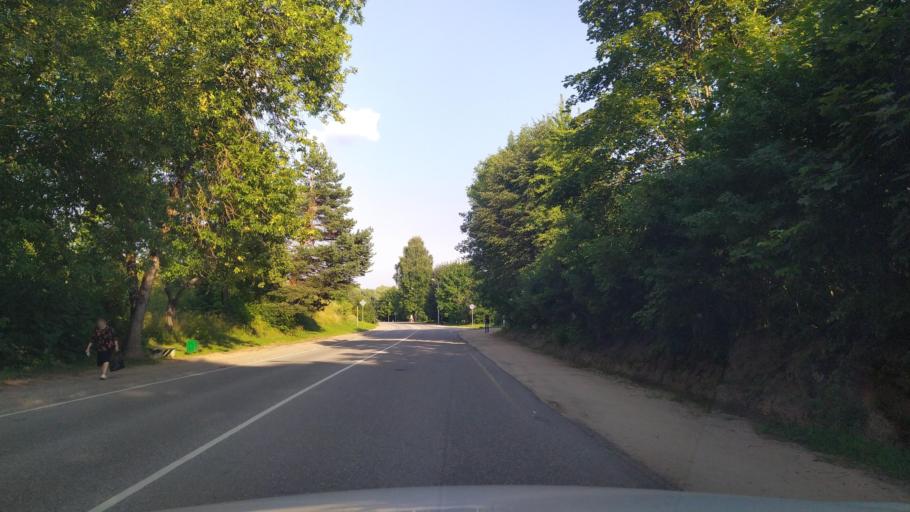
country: RU
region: Pskov
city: Pushkinskiye Gory
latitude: 57.0227
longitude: 28.9231
